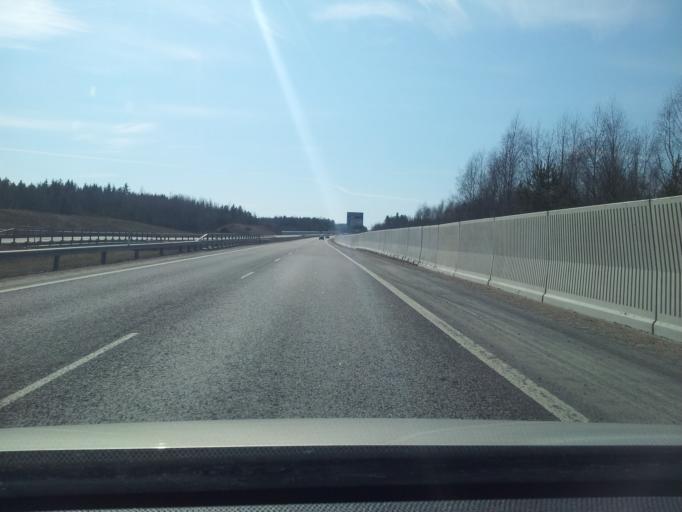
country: FI
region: Kymenlaakso
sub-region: Kotka-Hamina
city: Karhula
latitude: 60.5481
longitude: 26.9909
